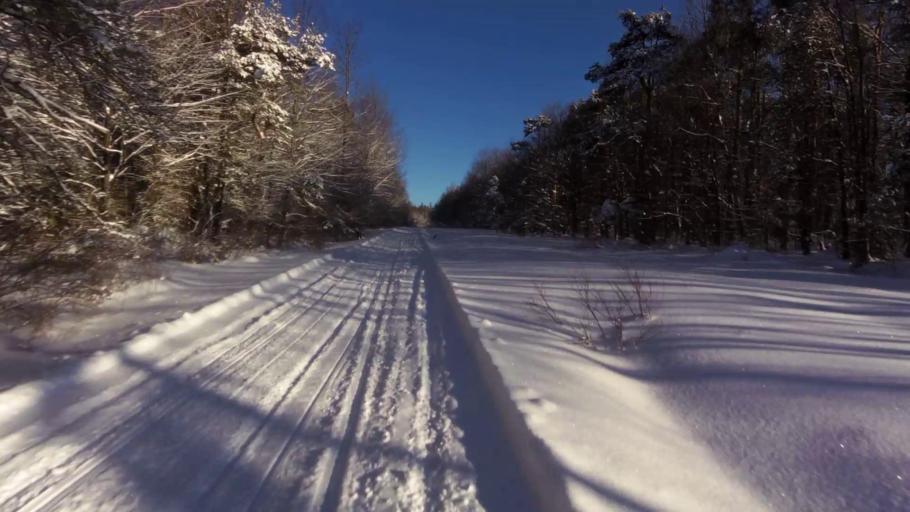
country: US
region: New York
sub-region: Chautauqua County
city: Falconer
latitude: 42.2359
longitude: -79.2177
